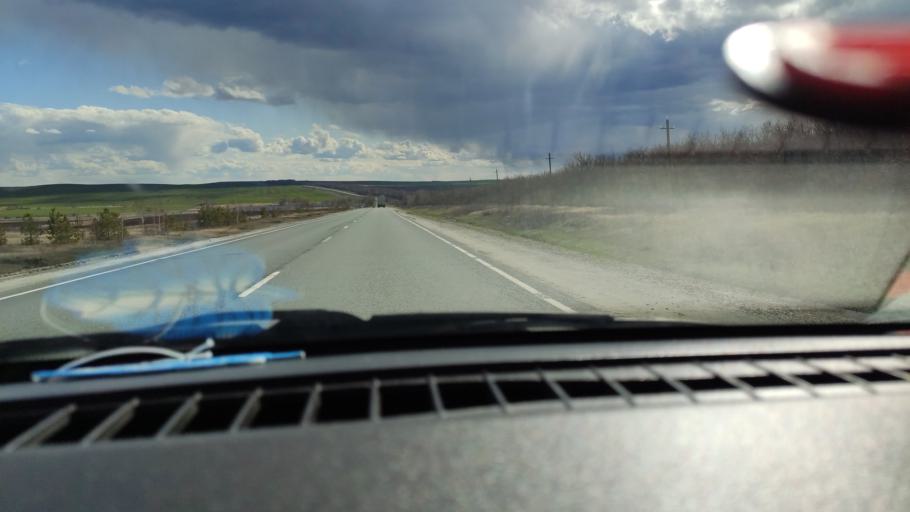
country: RU
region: Saratov
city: Alekseyevka
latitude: 52.2535
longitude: 47.9145
